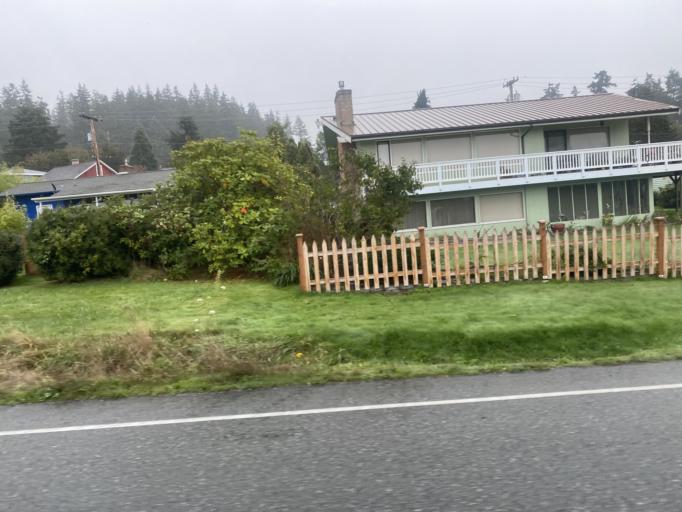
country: US
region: Washington
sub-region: Island County
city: Freeland
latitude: 48.0129
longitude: -122.5268
